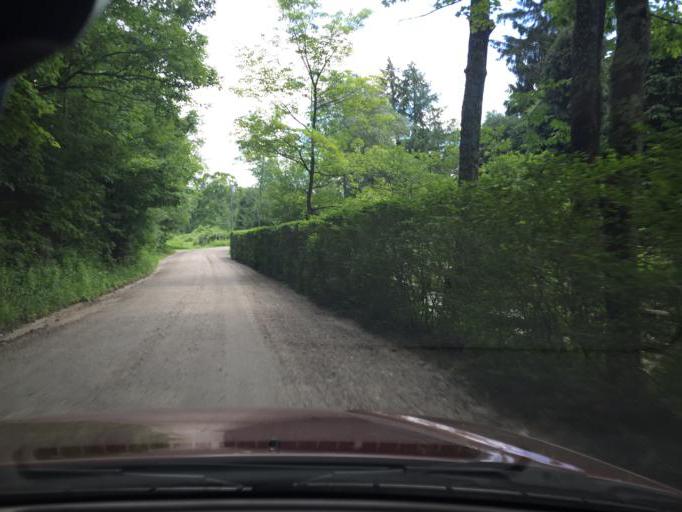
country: US
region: Connecticut
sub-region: Litchfield County
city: Litchfield
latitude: 41.7522
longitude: -73.2233
